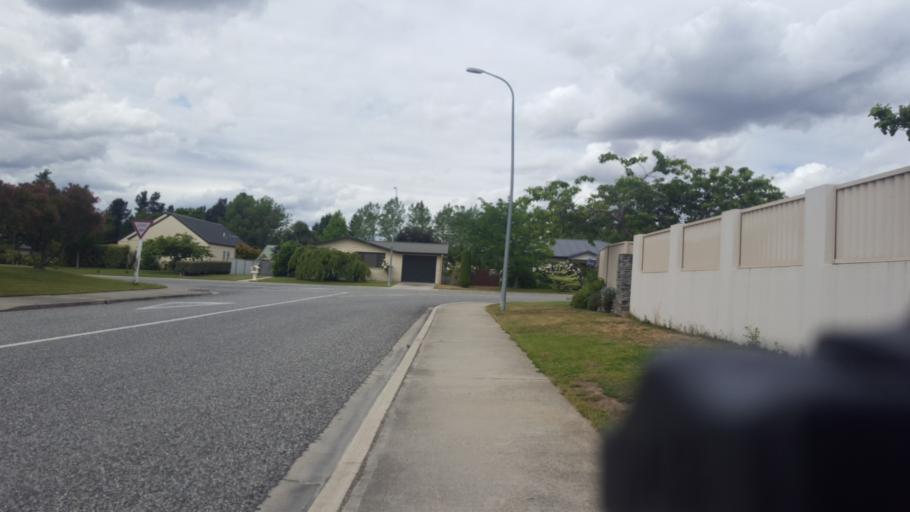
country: NZ
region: Otago
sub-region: Queenstown-Lakes District
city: Wanaka
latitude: -45.2448
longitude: 169.3765
